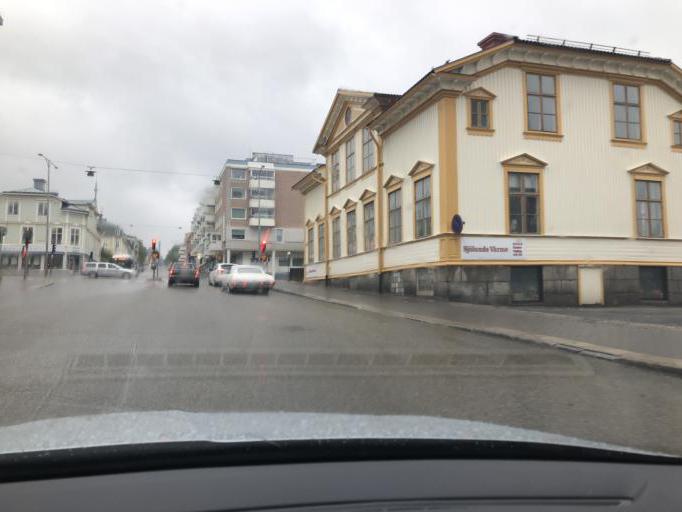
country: SE
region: Vaesternorrland
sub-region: OErnskoeldsviks Kommun
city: Ornskoldsvik
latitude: 63.2908
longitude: 18.7164
